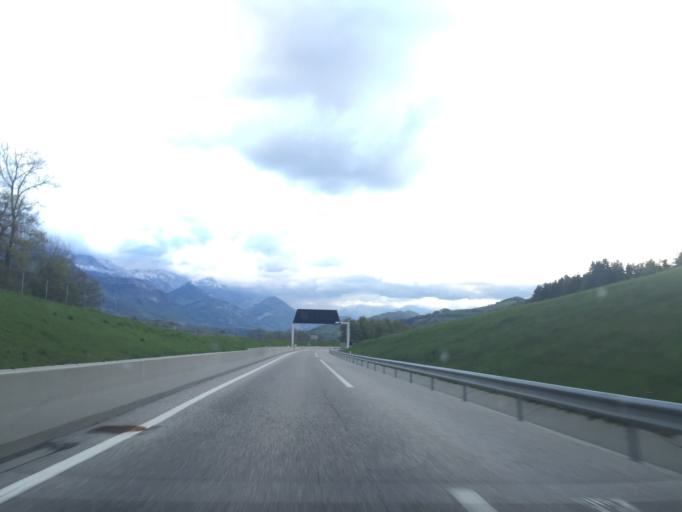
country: FR
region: Rhone-Alpes
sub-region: Departement de l'Isere
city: La Motte-Saint-Martin
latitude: 44.9220
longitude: 5.6300
